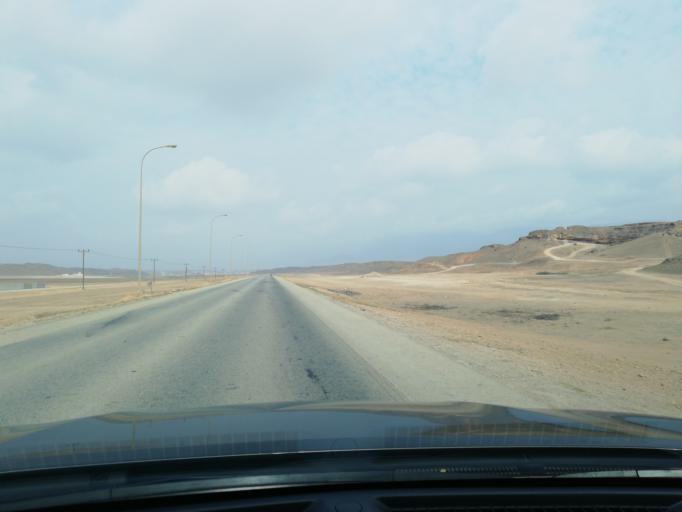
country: OM
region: Zufar
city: Salalah
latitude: 16.9580
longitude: 53.9011
